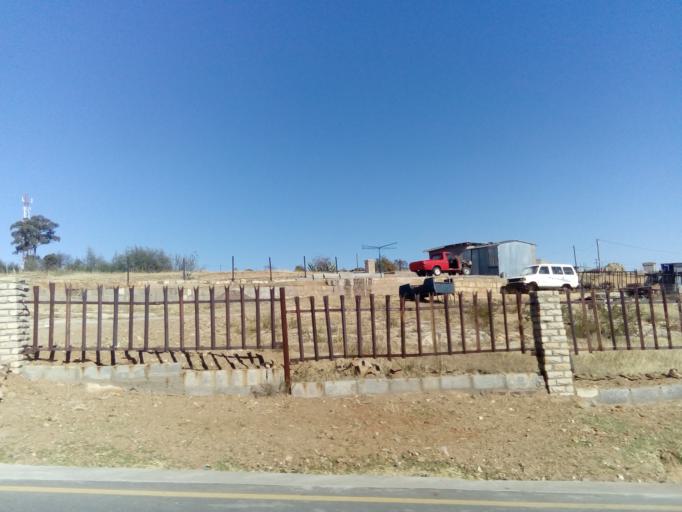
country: LS
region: Berea
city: Teyateyaneng
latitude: -29.1205
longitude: 27.8247
